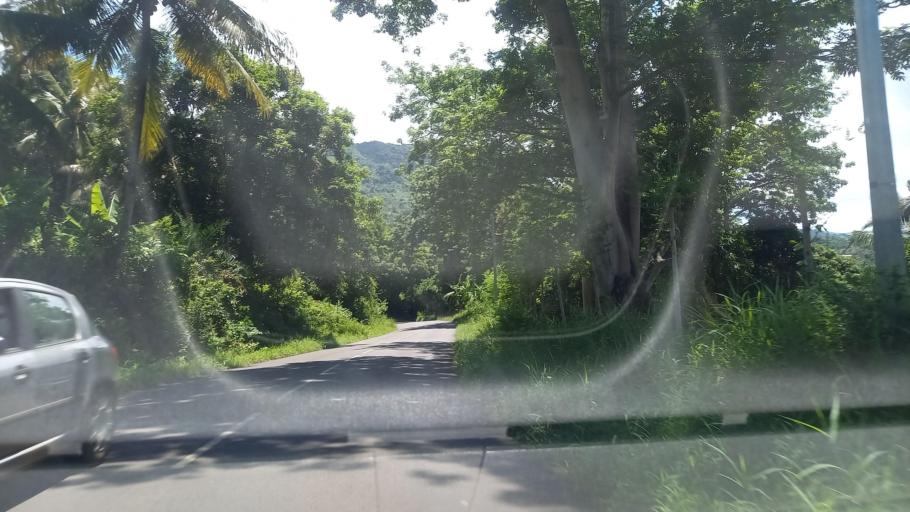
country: YT
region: Sada
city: Sada
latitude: -12.8619
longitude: 45.1086
